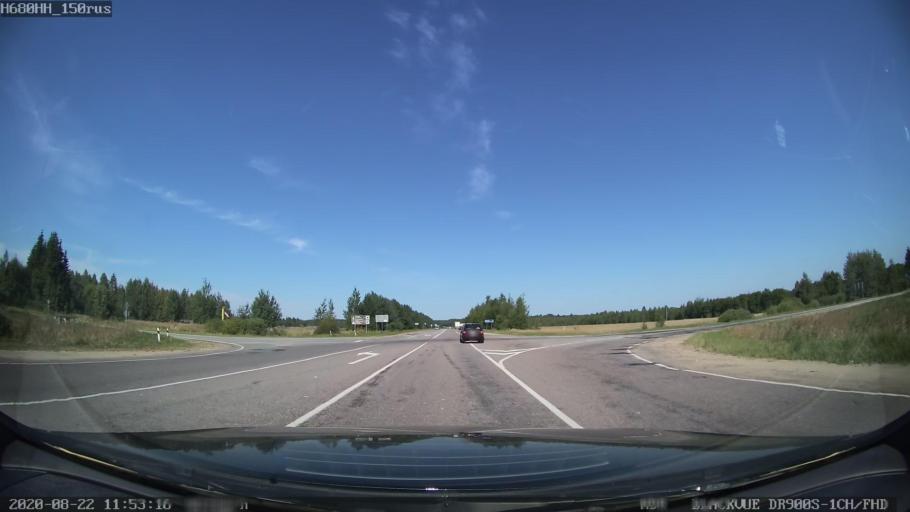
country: RU
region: Tverskaya
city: Vasil'yevskiy Mokh
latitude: 57.1249
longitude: 36.1123
